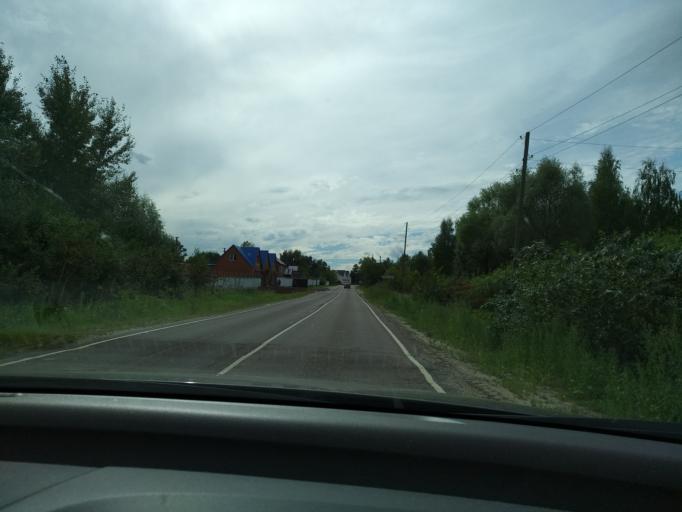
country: RU
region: Moskovskaya
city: Krasnyy Tkach
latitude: 55.3936
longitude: 39.1604
